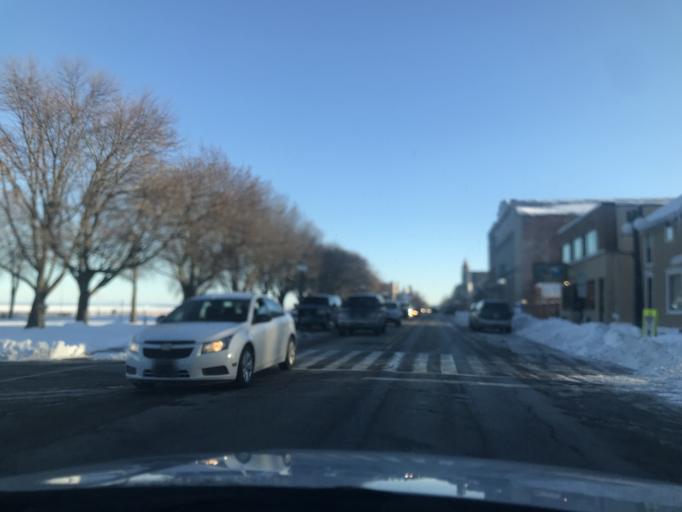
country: US
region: Michigan
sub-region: Menominee County
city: Menominee
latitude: 45.1059
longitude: -87.6041
